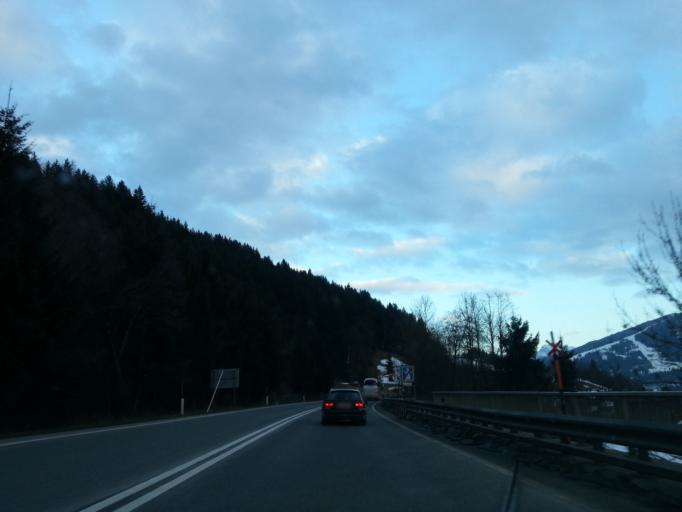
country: AT
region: Salzburg
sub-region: Politischer Bezirk Sankt Johann im Pongau
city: Eben im Pongau
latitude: 47.3923
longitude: 13.4075
